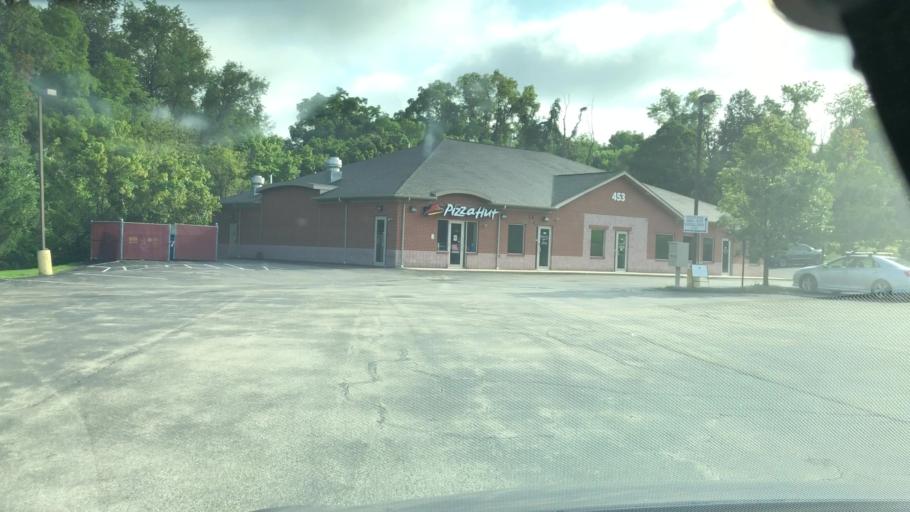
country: US
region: Pennsylvania
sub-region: Washington County
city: McMurray
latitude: 40.2804
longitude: -80.0841
